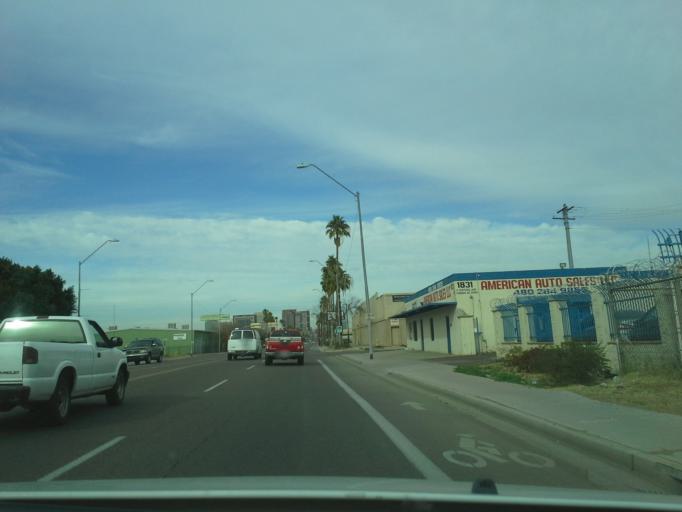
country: US
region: Arizona
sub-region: Maricopa County
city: Phoenix
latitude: 33.4289
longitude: -112.0736
